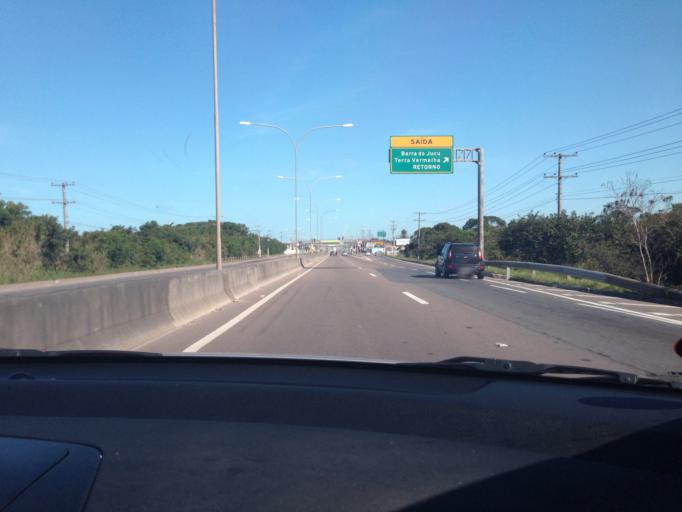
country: BR
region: Espirito Santo
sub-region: Vila Velha
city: Vila Velha
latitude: -20.4166
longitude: -40.3282
